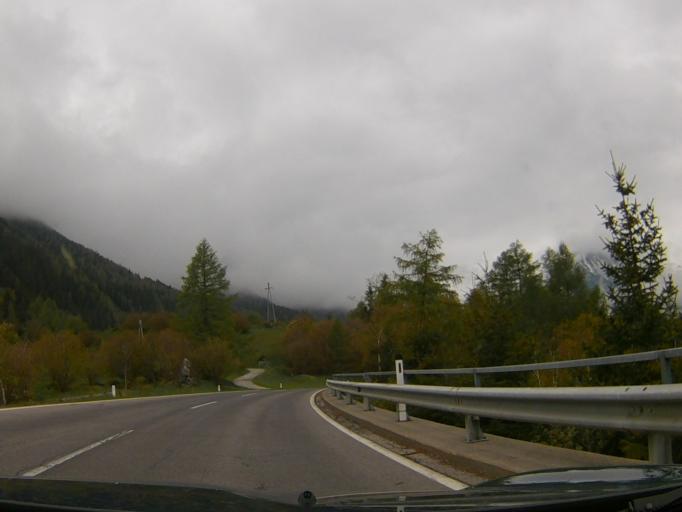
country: AT
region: Carinthia
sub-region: Politischer Bezirk Spittal an der Drau
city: Obervellach
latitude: 46.9708
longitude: 13.1825
